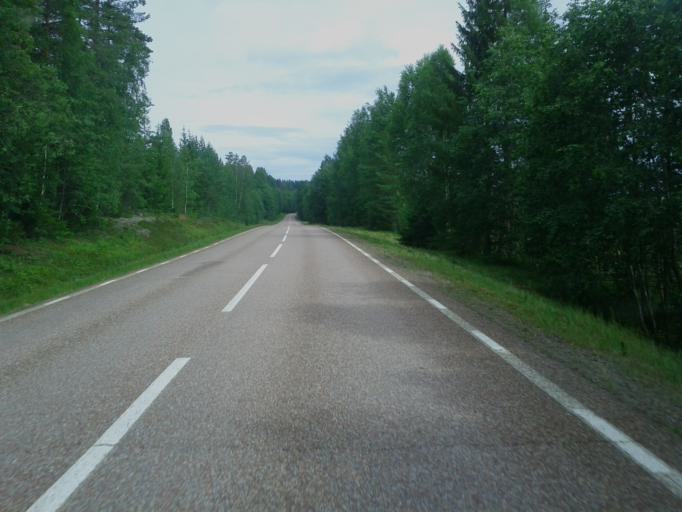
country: SE
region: Dalarna
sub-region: Borlange Kommun
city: Borlaenge
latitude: 60.3246
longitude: 15.3838
